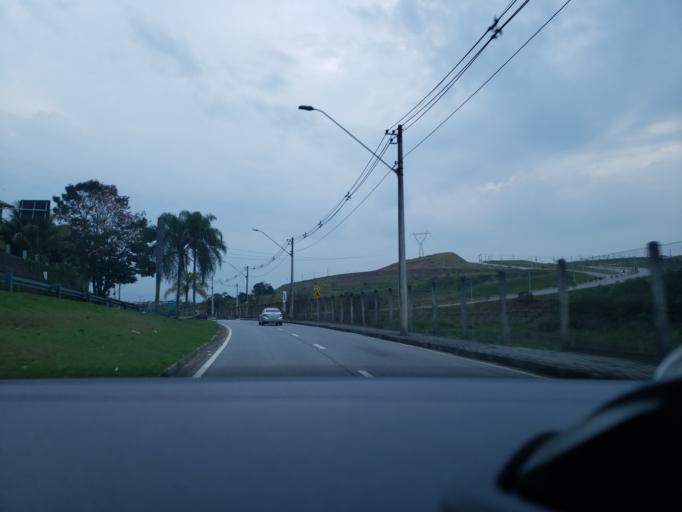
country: BR
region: Sao Paulo
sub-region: Sao Jose Dos Campos
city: Sao Jose dos Campos
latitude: -23.1912
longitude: -45.9356
